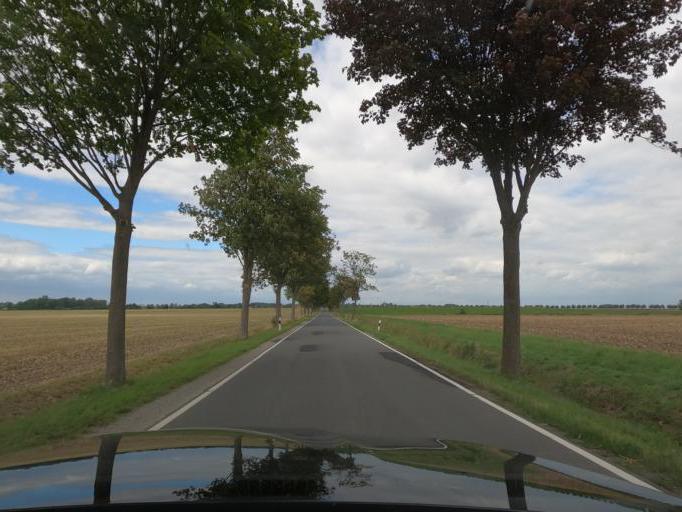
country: DE
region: Lower Saxony
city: Hohenhameln
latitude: 52.2283
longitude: 10.0633
